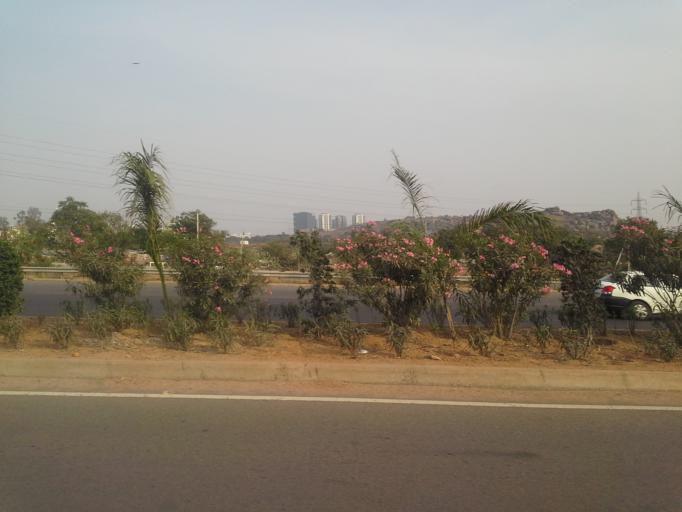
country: IN
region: Telangana
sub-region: Rangareddi
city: Kukatpalli
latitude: 17.4143
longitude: 78.3552
